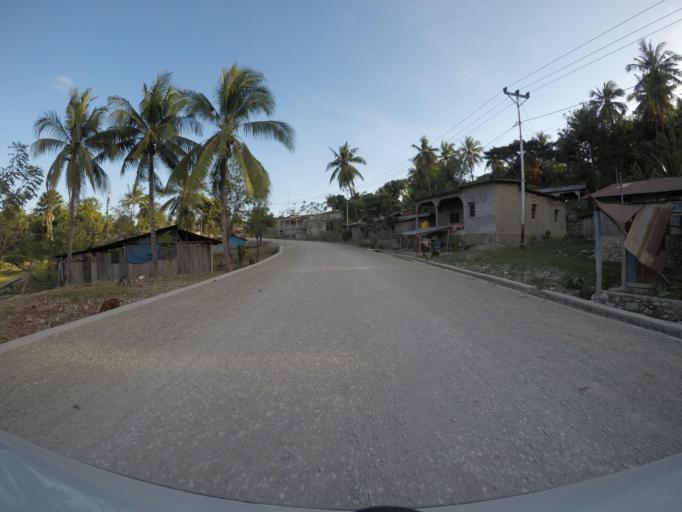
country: TL
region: Viqueque
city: Viqueque
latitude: -8.8200
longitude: 126.5329
